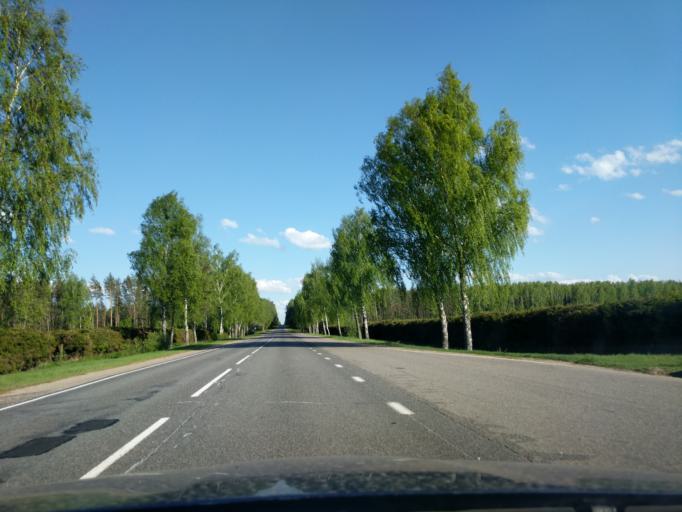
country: BY
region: Minsk
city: Myadzyel
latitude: 54.8146
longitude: 26.9719
